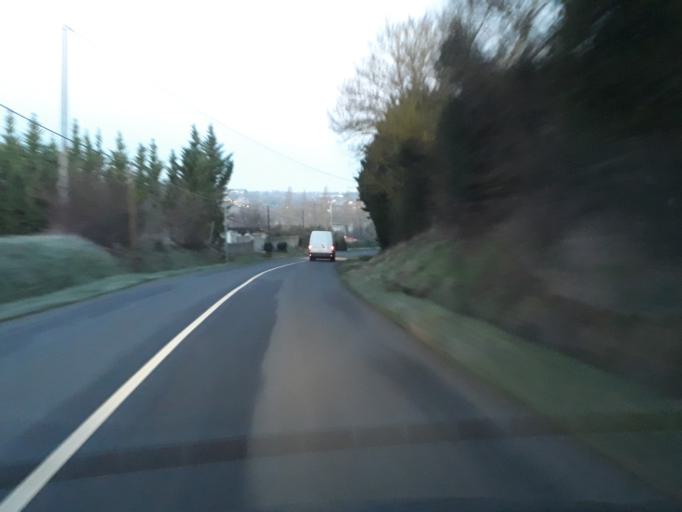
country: FR
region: Midi-Pyrenees
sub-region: Departement du Gers
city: Samatan
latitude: 43.4805
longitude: 0.9382
